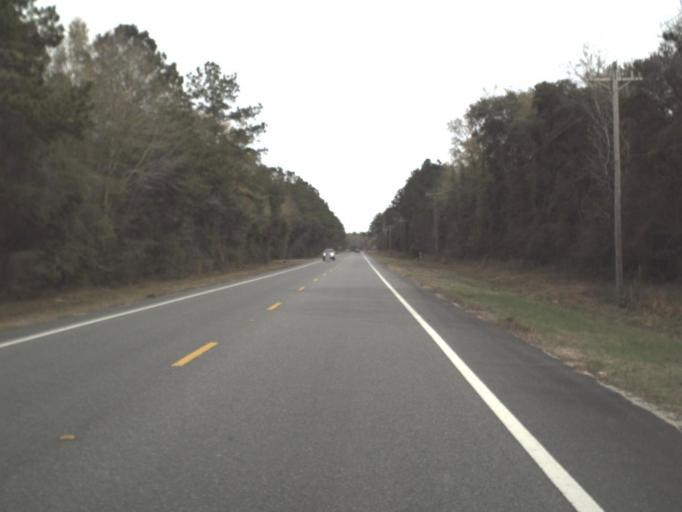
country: US
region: Florida
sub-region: Wakulla County
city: Crawfordville
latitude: 30.2549
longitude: -84.3363
